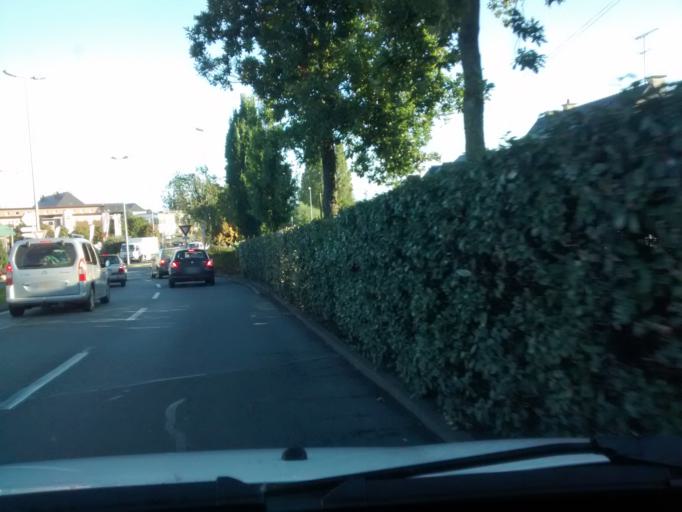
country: FR
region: Brittany
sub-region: Departement d'Ille-et-Vilaine
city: Saint-Malo
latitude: 48.6350
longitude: -1.9895
